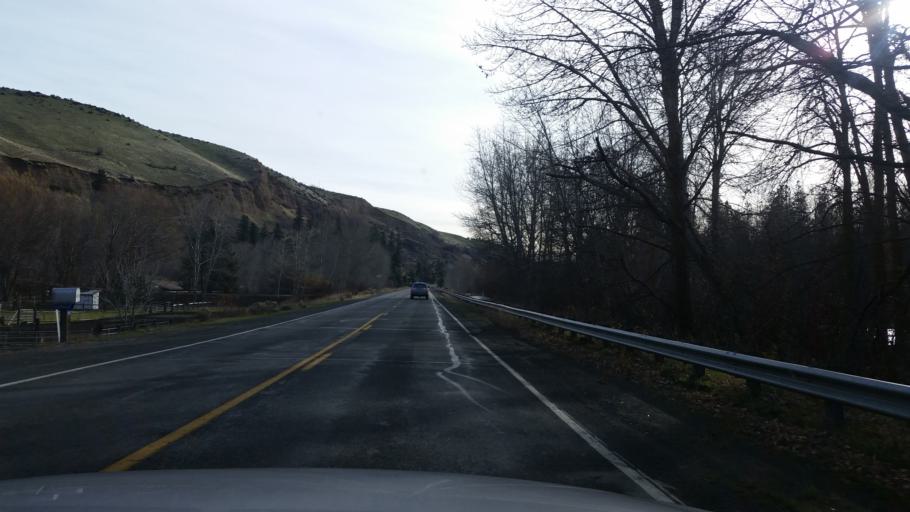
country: US
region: Washington
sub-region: Kittitas County
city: Ellensburg
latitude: 47.0770
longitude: -120.6667
